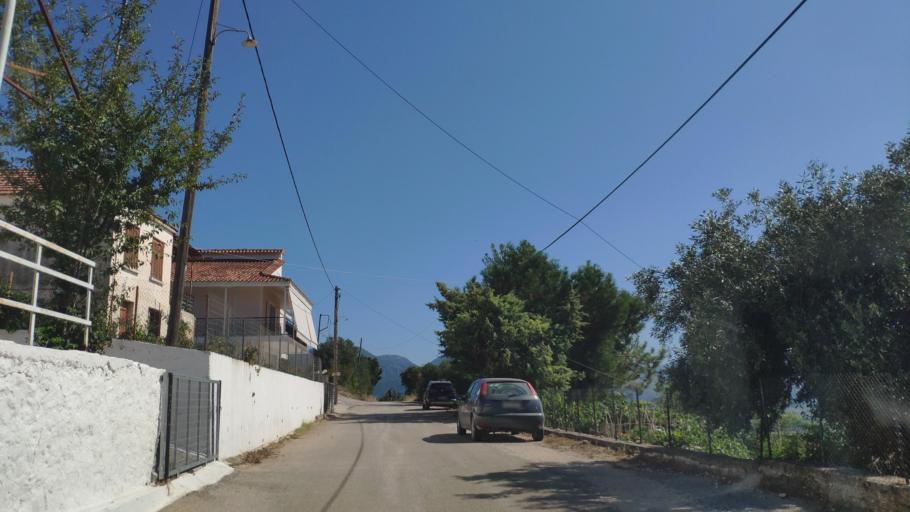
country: GR
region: Epirus
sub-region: Nomos Prevezis
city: Kanalaki
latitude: 39.2745
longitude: 20.5993
